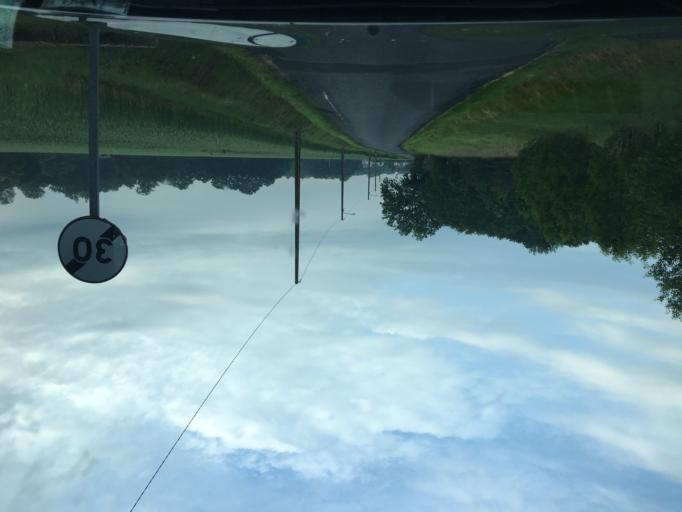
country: FR
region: Centre
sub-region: Departement du Loiret
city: Saint-Denis-en-Val
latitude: 47.8848
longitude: 1.9512
